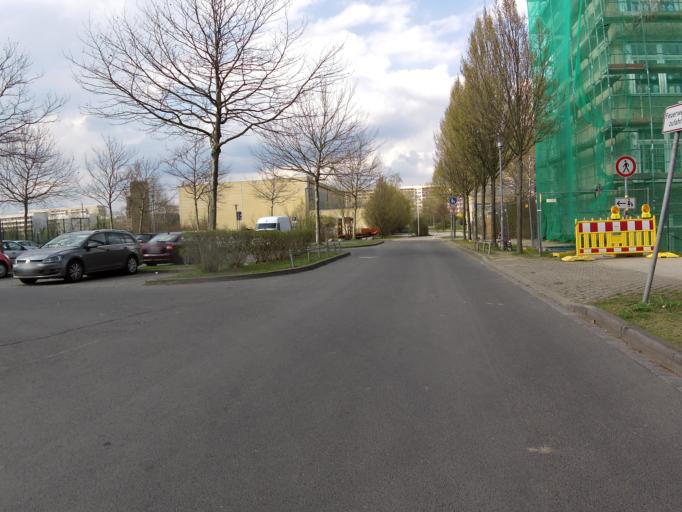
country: DE
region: Saxony
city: Markranstadt
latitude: 51.3137
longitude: 12.2914
